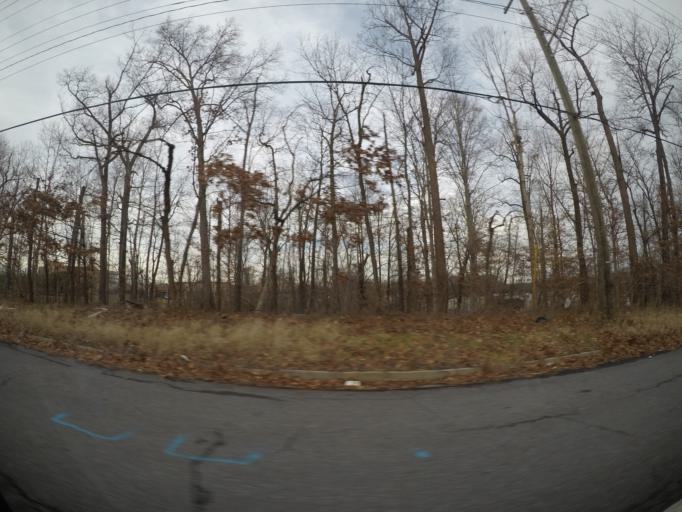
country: US
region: Maryland
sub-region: Howard County
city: Hanover
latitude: 39.1820
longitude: -76.7526
